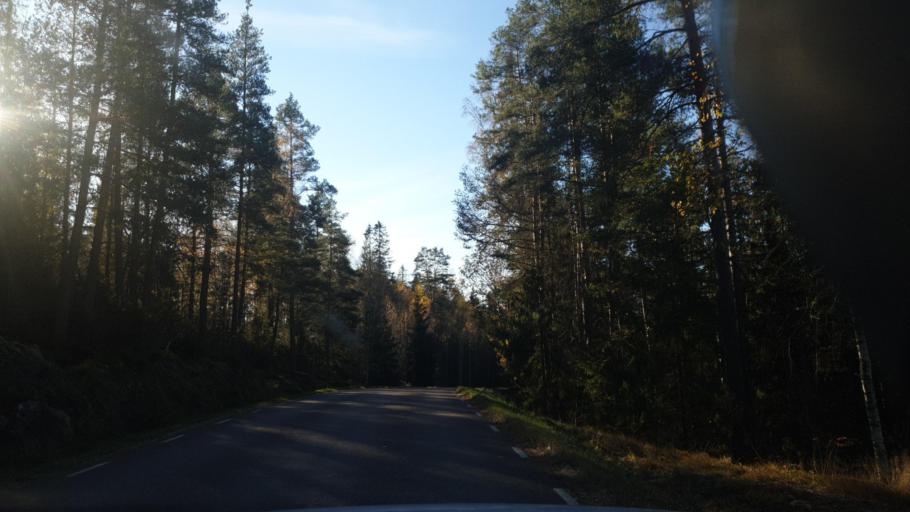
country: SE
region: Vaermland
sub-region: Grums Kommun
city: Grums
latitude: 59.4208
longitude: 13.0867
